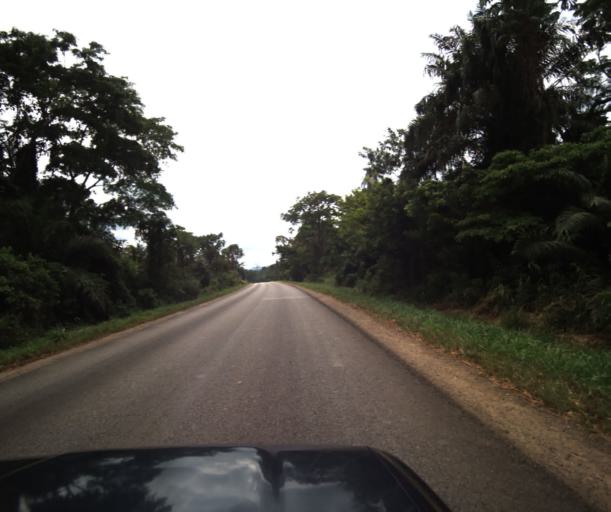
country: CM
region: Centre
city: Eseka
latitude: 3.8501
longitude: 10.4892
